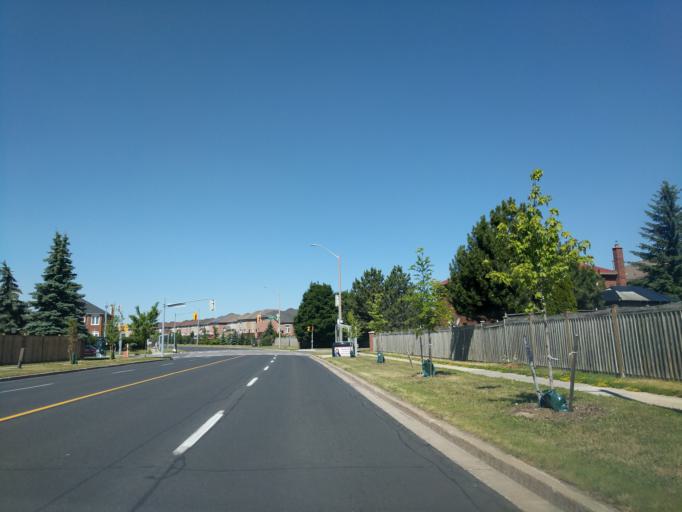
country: CA
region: Ontario
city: Markham
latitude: 43.8423
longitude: -79.2728
